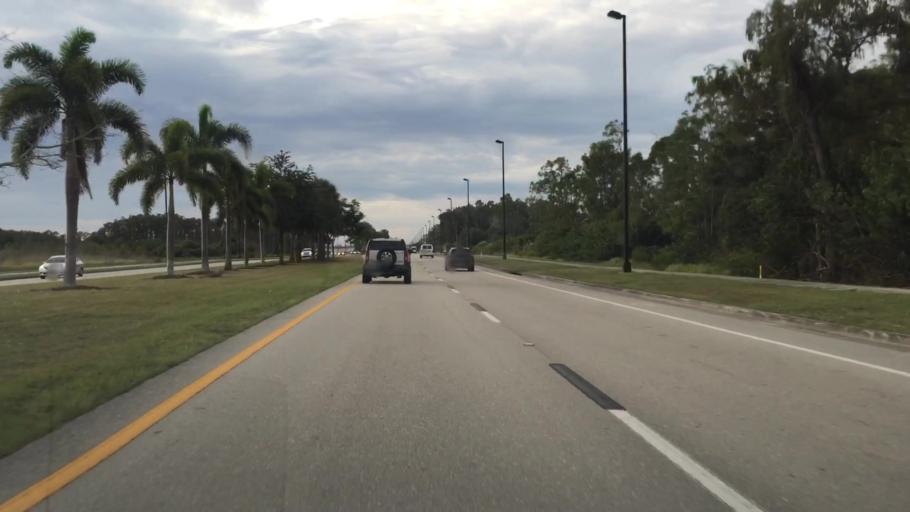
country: US
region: Florida
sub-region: Lee County
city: Three Oaks
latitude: 26.5251
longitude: -81.7856
